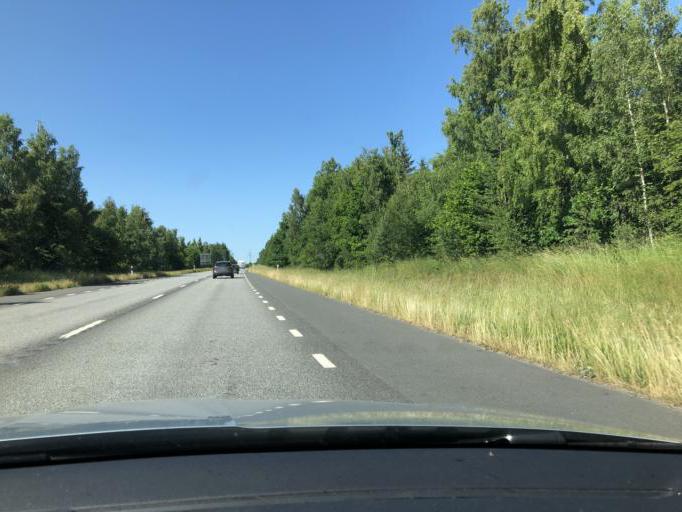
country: SE
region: Skane
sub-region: Bromolla Kommun
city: Bromoella
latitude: 56.0701
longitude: 14.4987
